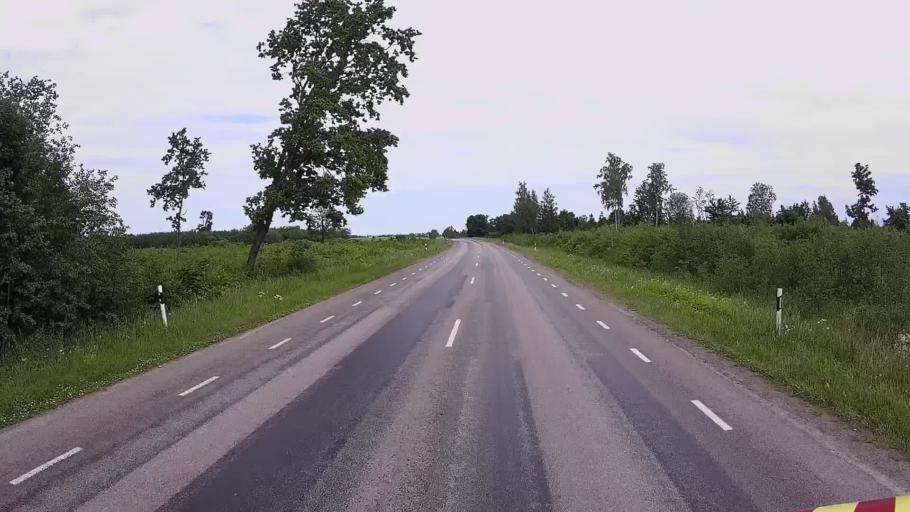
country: EE
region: Laeaene-Virumaa
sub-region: Vaeike-Maarja vald
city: Vaike-Maarja
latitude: 59.1472
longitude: 26.2633
